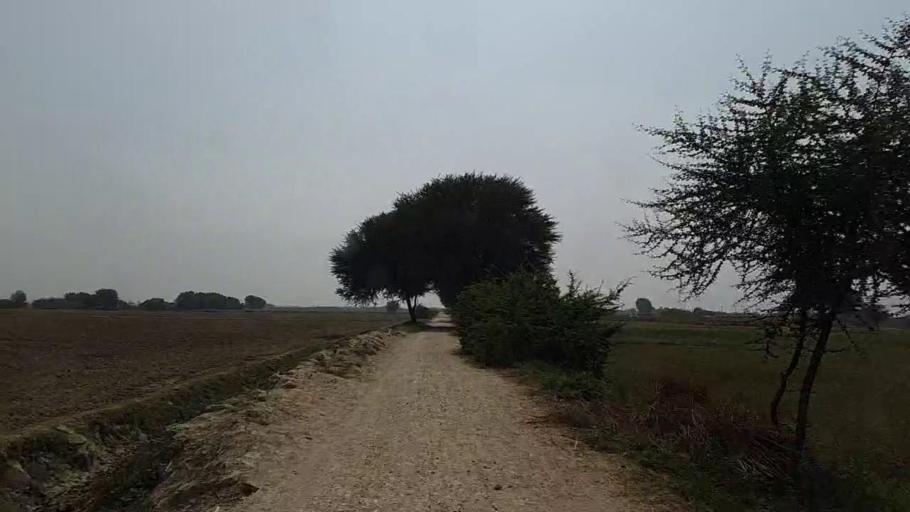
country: PK
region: Sindh
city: Naukot
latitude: 24.8182
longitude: 69.3595
